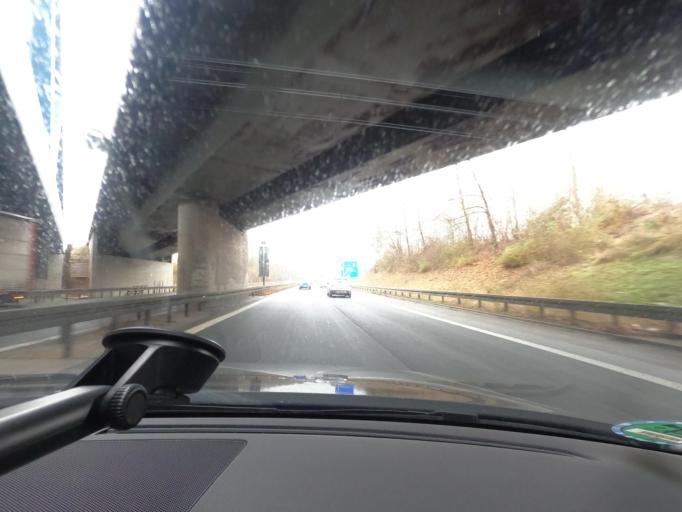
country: DE
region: Bavaria
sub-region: Upper Franconia
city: Eggolsheim
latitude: 49.7469
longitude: 11.0591
